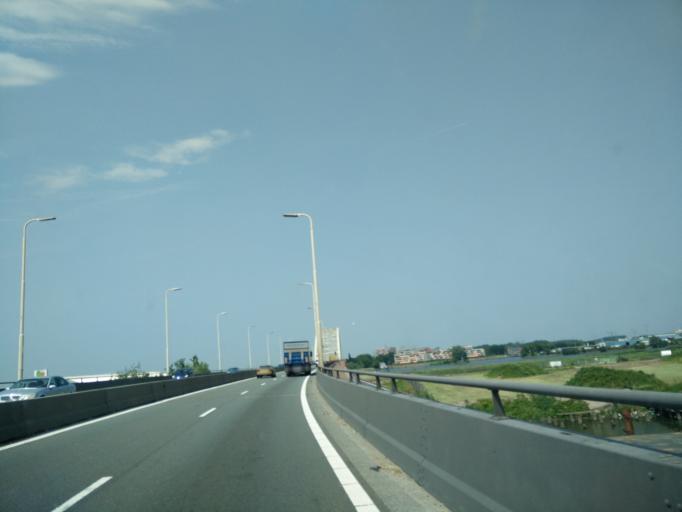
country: NL
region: South Holland
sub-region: Gemeente Papendrecht
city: Papendrecht
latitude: 51.8187
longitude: 4.7066
